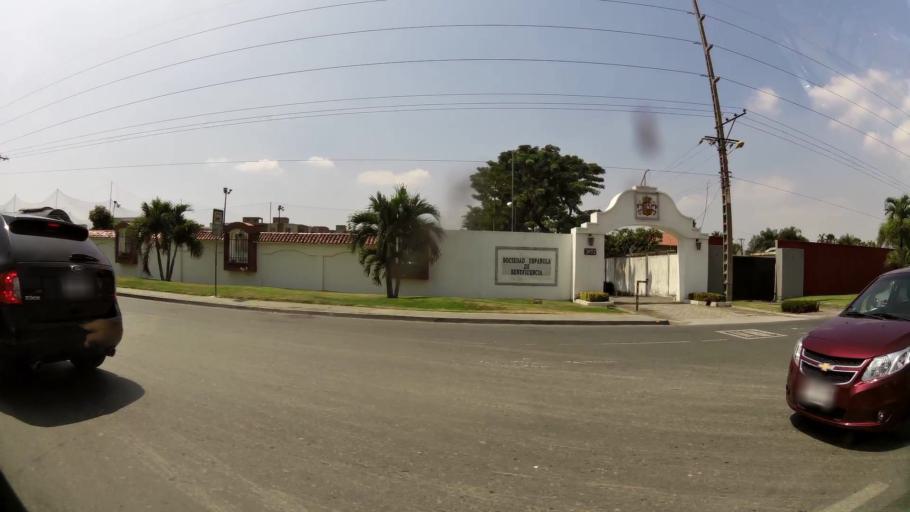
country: EC
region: Guayas
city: Eloy Alfaro
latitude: -2.1231
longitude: -79.8647
